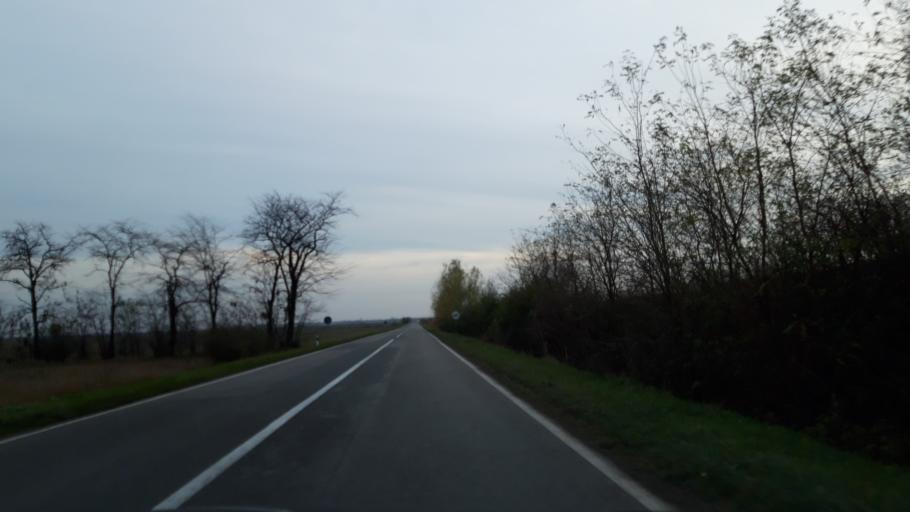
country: RS
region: Autonomna Pokrajina Vojvodina
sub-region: Severnobanatski Okrug
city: Coka
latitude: 45.9253
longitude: 20.1456
